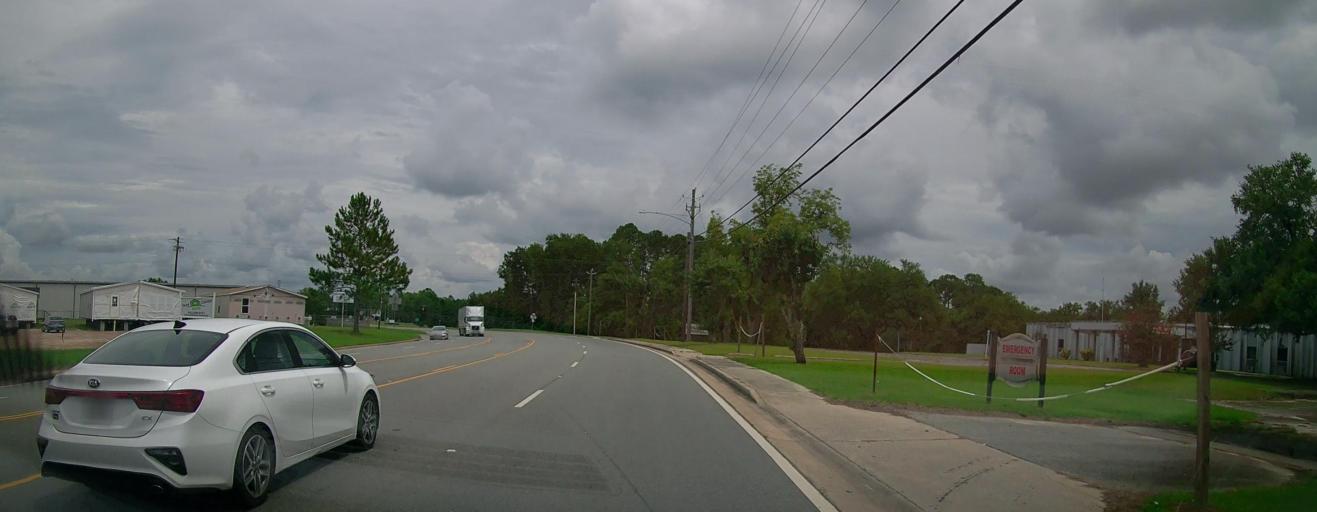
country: US
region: Georgia
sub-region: Telfair County
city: McRae
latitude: 32.0605
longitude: -82.8816
